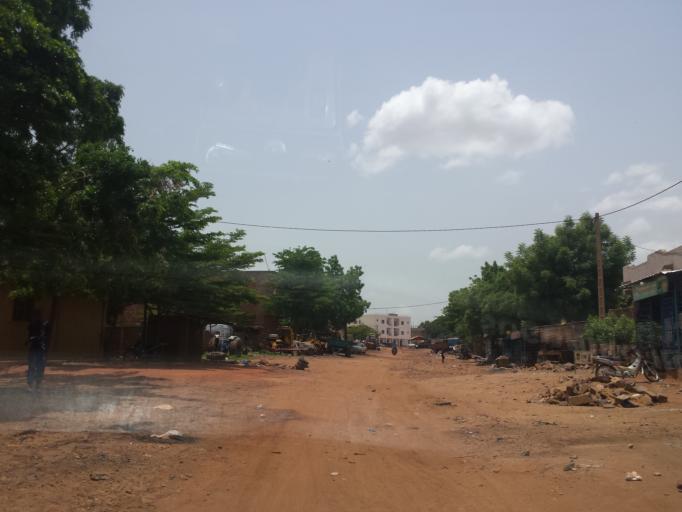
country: ML
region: Bamako
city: Bamako
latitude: 12.6081
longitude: -7.9628
